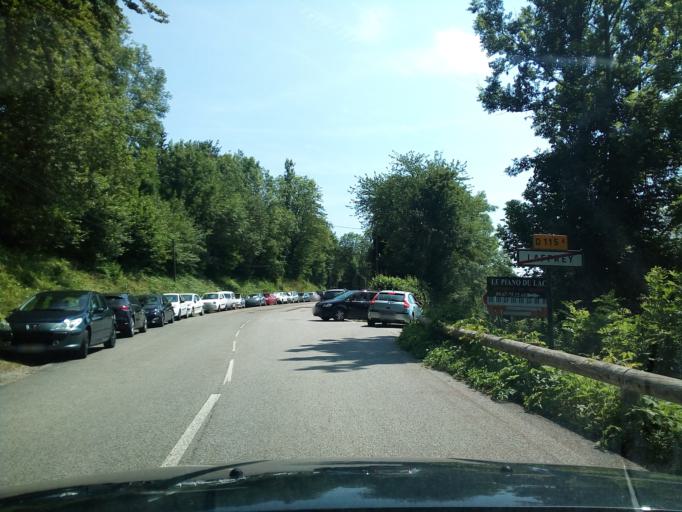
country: FR
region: Rhone-Alpes
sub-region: Departement de l'Isere
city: Notre-Dame-de-Mesage
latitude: 45.0224
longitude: 5.7835
